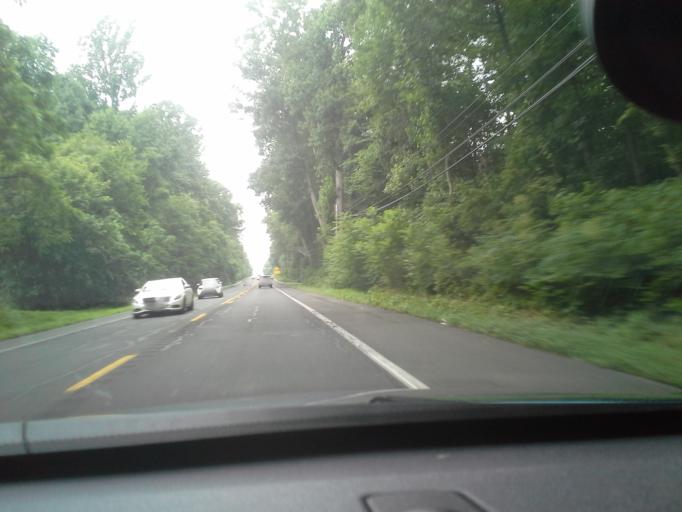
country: US
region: Maryland
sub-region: Calvert County
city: Dunkirk Town Center
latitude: 38.7454
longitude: -76.6356
